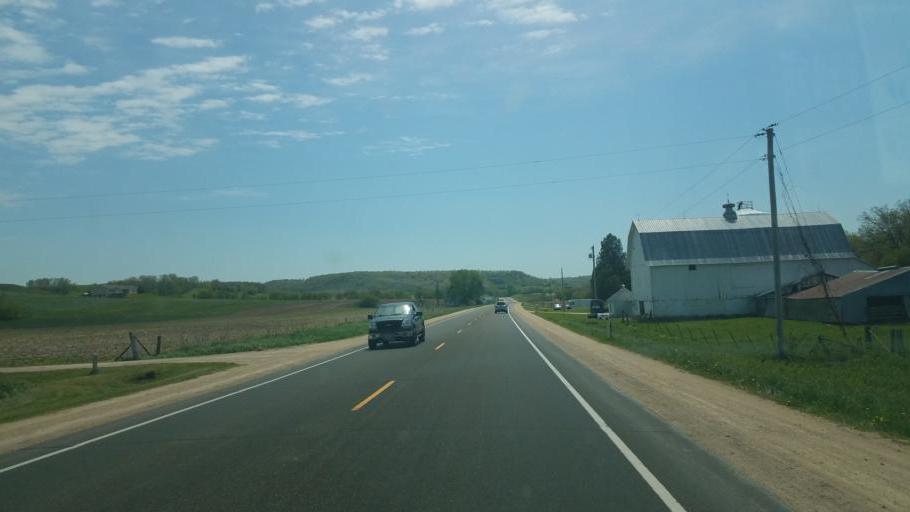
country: US
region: Wisconsin
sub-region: Monroe County
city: Tomah
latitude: 43.8460
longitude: -90.4738
